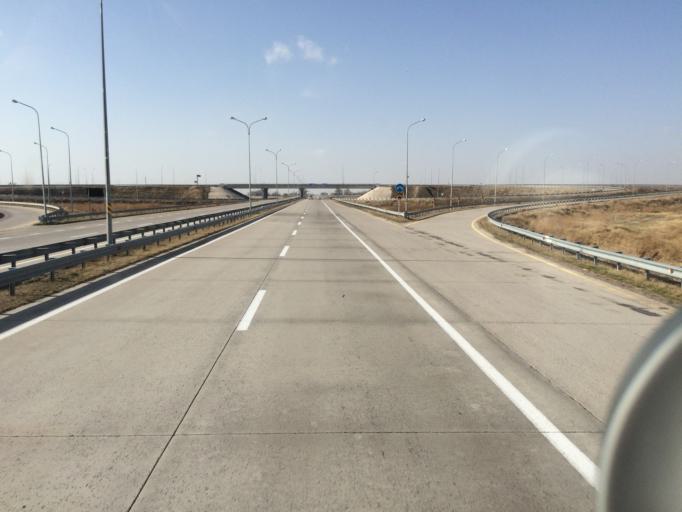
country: KZ
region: Zhambyl
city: Oytal
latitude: 42.9283
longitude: 73.2465
